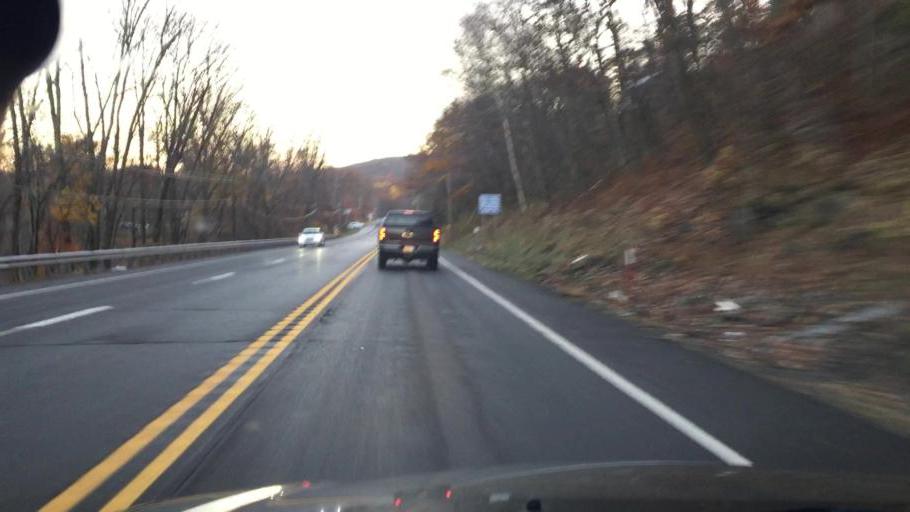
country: US
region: Pennsylvania
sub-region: Luzerne County
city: Freeland
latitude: 41.0896
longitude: -75.9427
